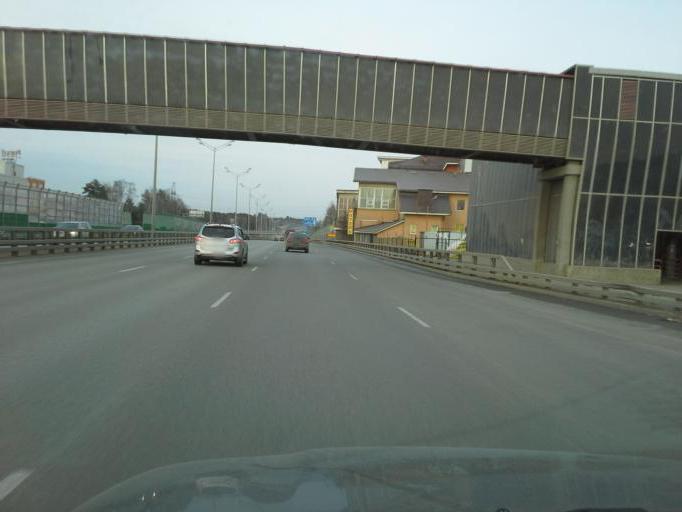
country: RU
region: Moskovskaya
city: Lesnoy Gorodok
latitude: 55.6365
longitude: 37.2224
